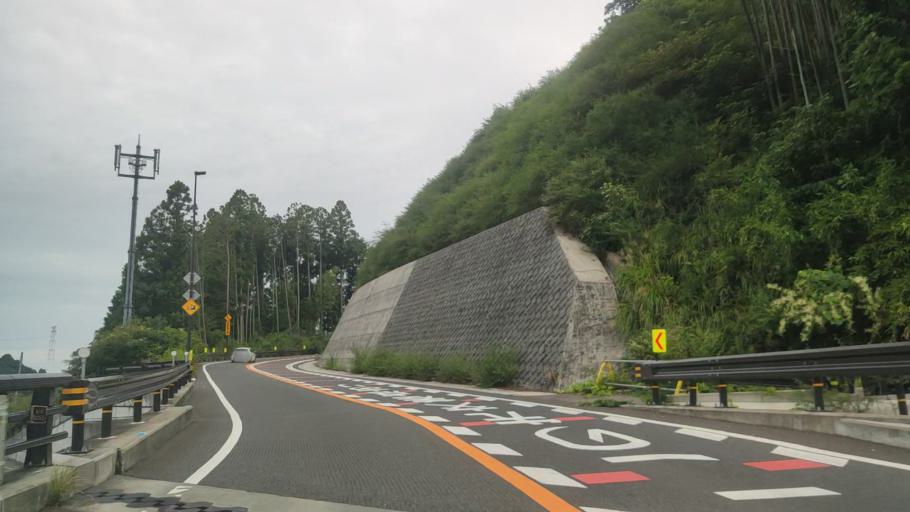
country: JP
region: Wakayama
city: Hashimoto
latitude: 34.3944
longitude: 135.5959
